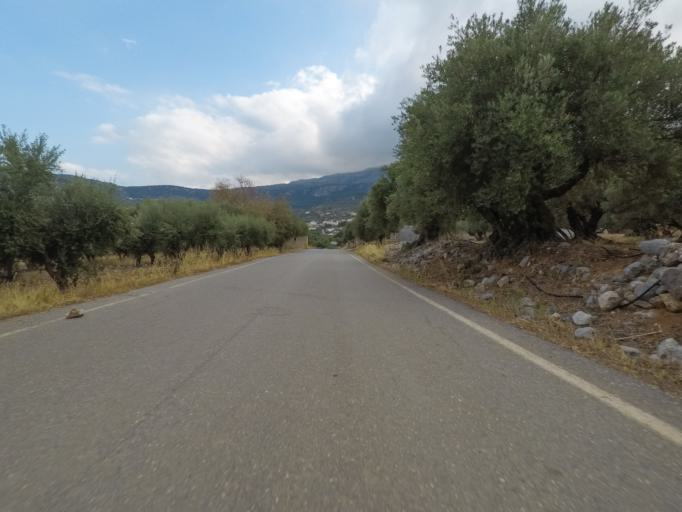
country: GR
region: Crete
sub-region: Nomos Lasithiou
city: Kritsa
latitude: 35.1621
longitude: 25.6514
